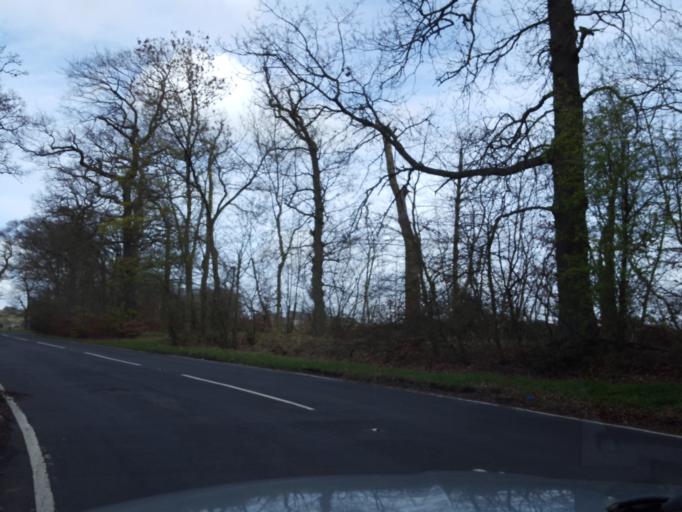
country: GB
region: Scotland
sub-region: West Lothian
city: Bathgate
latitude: 55.9366
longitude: -3.6619
